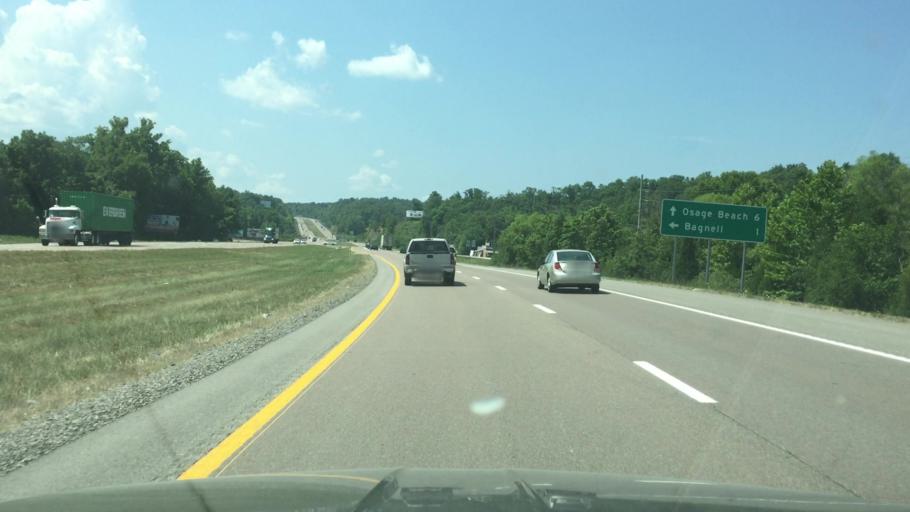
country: US
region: Missouri
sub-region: Miller County
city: Lake Ozark
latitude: 38.2400
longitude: -92.6180
